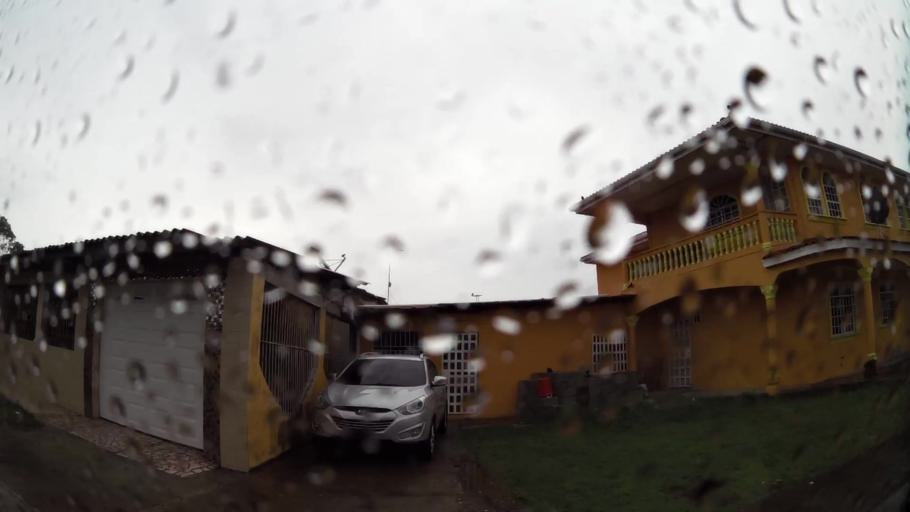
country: PA
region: Colon
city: Arco Iris
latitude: 9.3416
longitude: -79.8920
